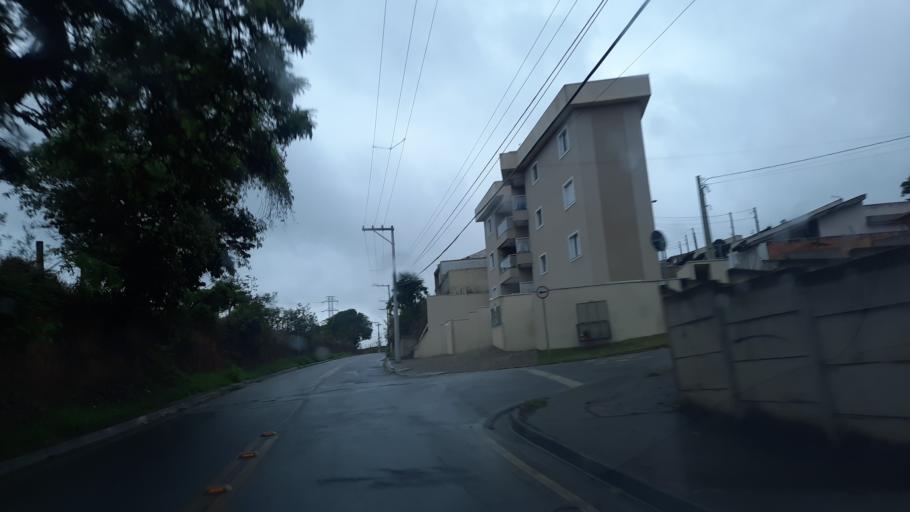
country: BR
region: Sao Paulo
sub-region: Atibaia
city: Atibaia
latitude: -23.0931
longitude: -46.5412
